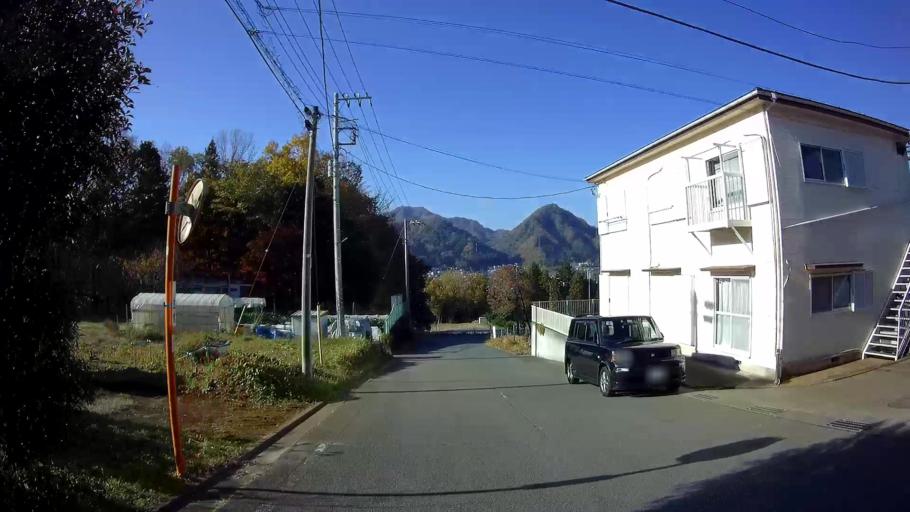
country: JP
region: Yamanashi
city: Uenohara
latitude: 35.6155
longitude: 139.1289
